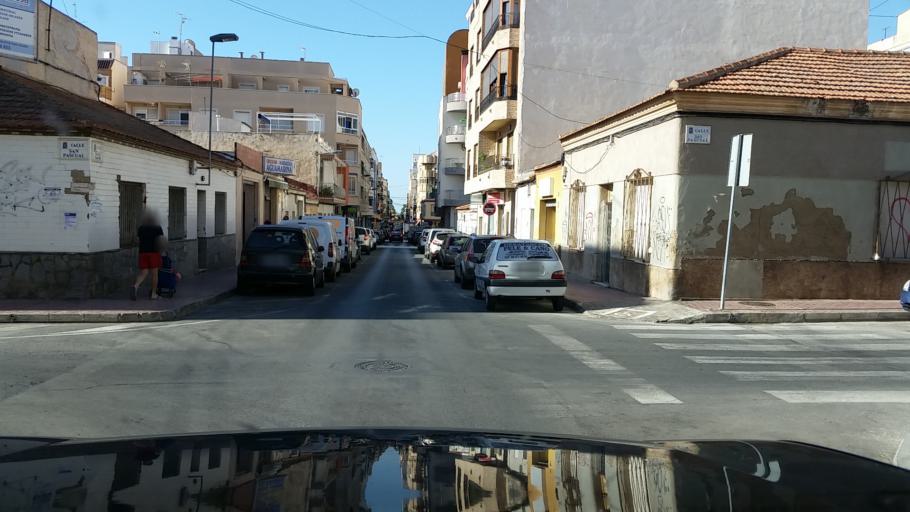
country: ES
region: Valencia
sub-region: Provincia de Alicante
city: Torrevieja
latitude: 37.9801
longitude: -0.6809
